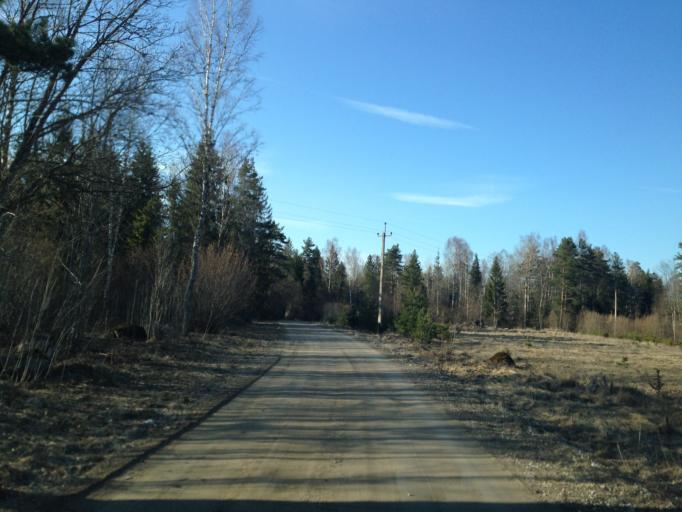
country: EE
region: Harju
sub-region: Nissi vald
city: Turba
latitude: 59.1293
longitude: 24.1657
